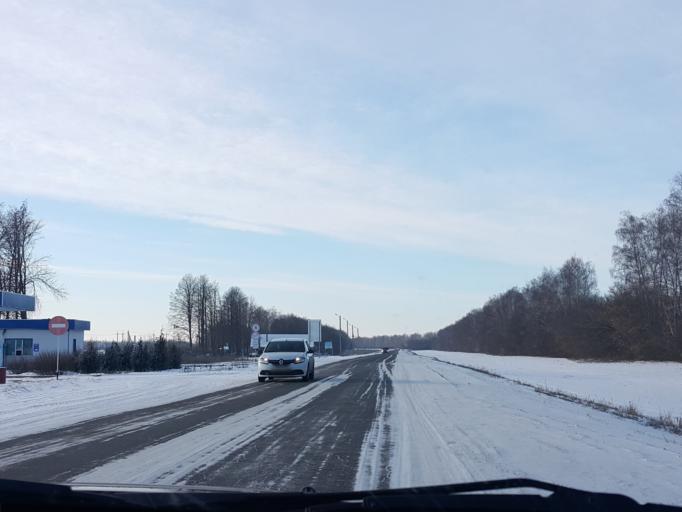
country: RU
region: Tambov
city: Znamenka
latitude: 52.4023
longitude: 41.3882
